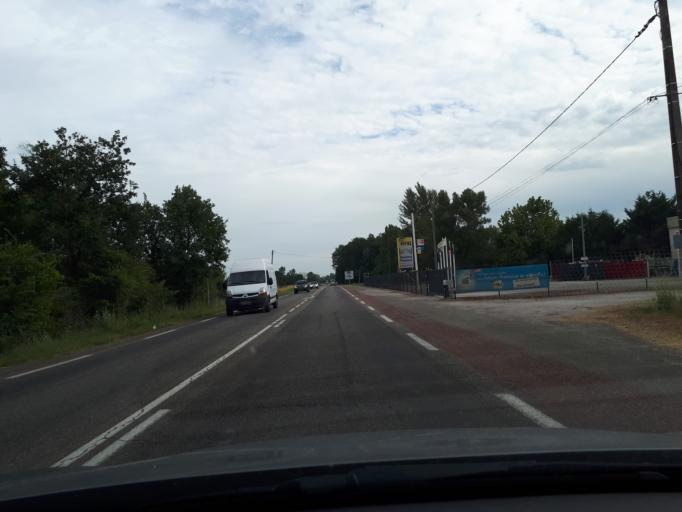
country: FR
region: Midi-Pyrenees
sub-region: Departement du Tarn-et-Garonne
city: Campsas
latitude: 43.9084
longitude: 1.3118
